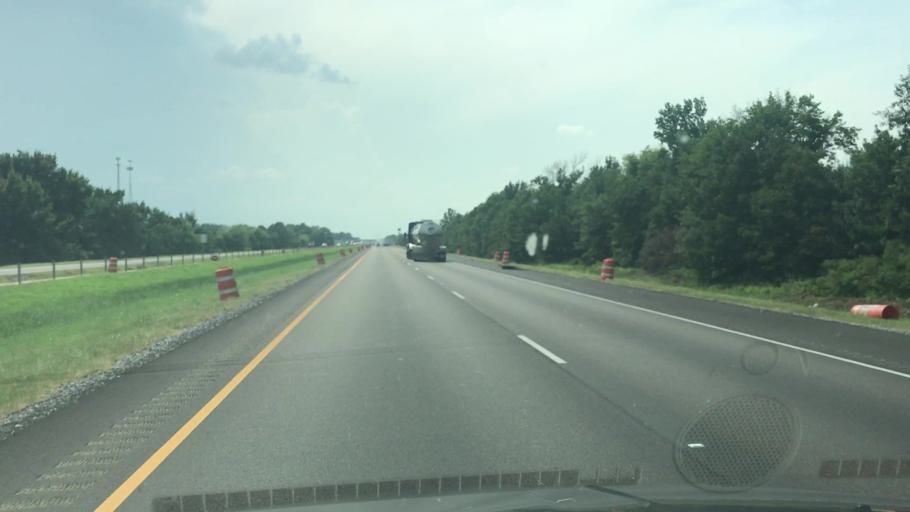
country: US
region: Arkansas
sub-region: Crittenden County
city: Earle
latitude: 35.1333
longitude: -90.4716
